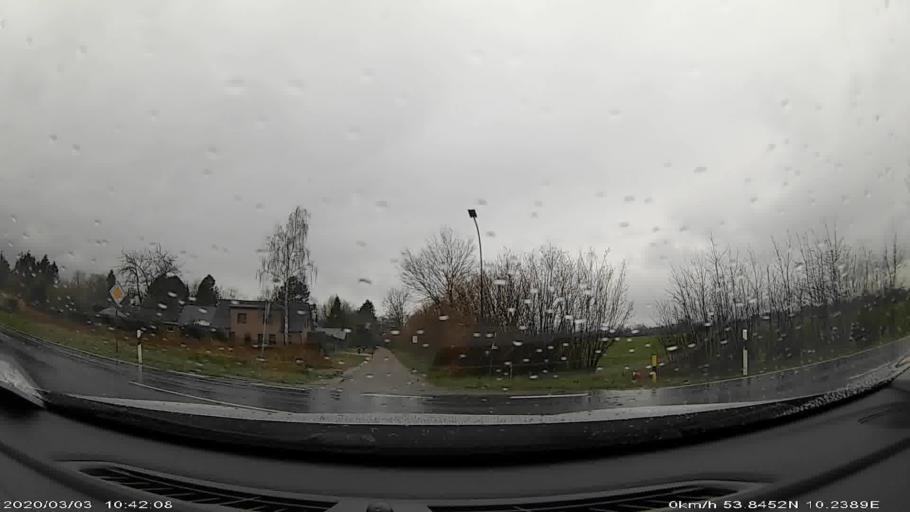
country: DE
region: Schleswig-Holstein
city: Gross Niendorf
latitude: 53.8440
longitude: 10.2375
